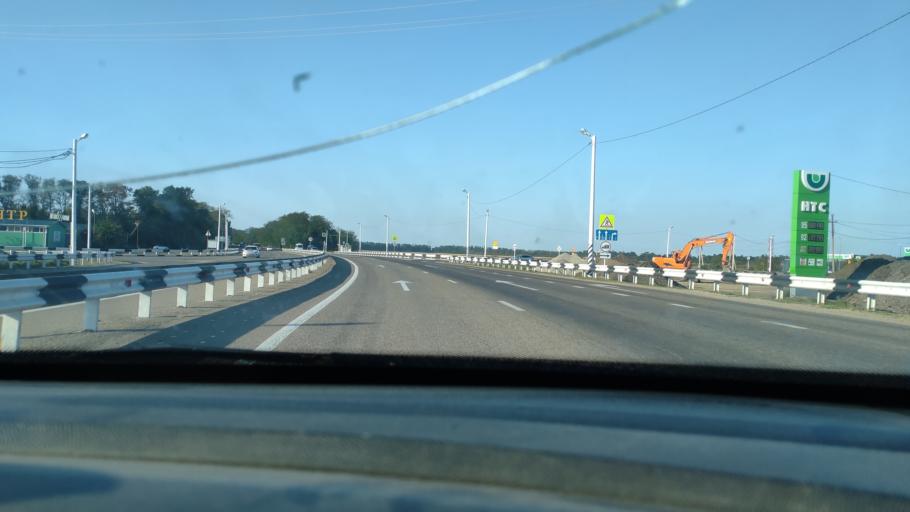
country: RU
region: Krasnodarskiy
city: Timashevsk
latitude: 45.5207
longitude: 38.9424
